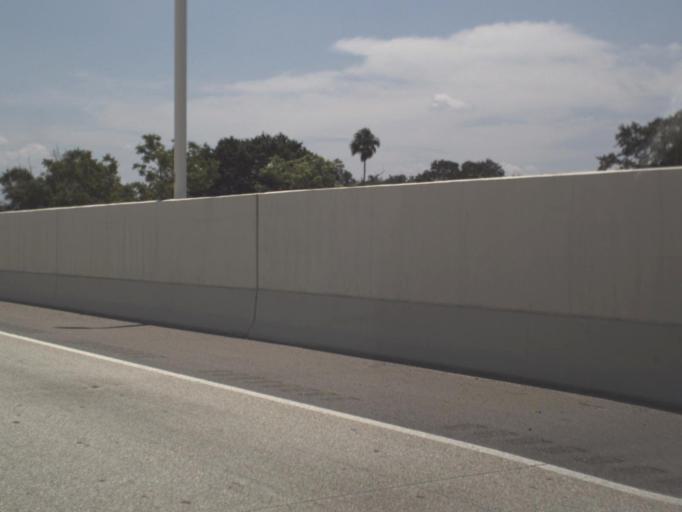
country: US
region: Florida
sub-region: Hillsborough County
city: Tampa
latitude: 27.9556
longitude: -82.4924
